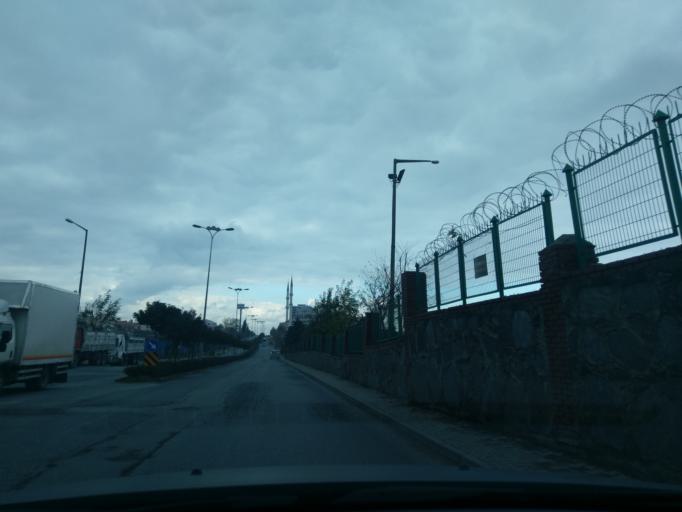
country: TR
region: Istanbul
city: Basaksehir
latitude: 41.0778
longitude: 28.7989
